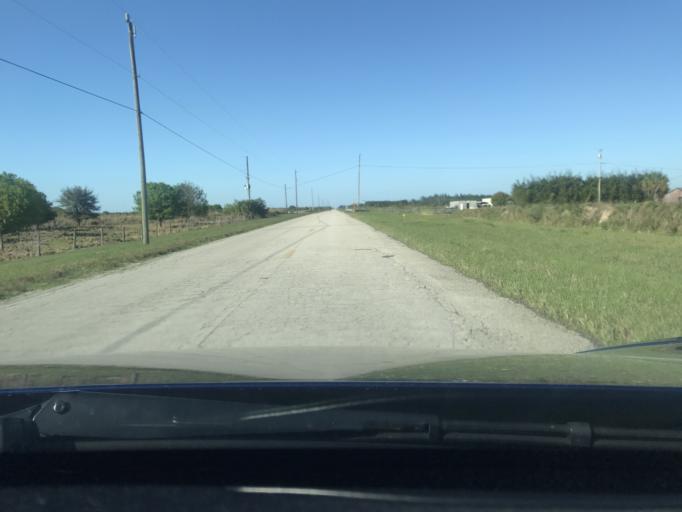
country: US
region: Florida
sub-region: Saint Lucie County
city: Fort Pierce South
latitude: 27.3879
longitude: -80.4975
